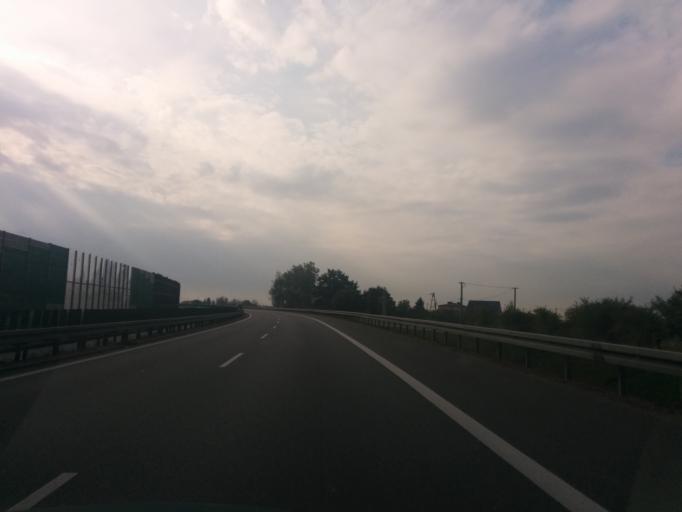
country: PL
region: Masovian Voivodeship
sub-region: Powiat bialobrzeski
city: Stara Blotnica
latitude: 51.5617
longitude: 21.0264
